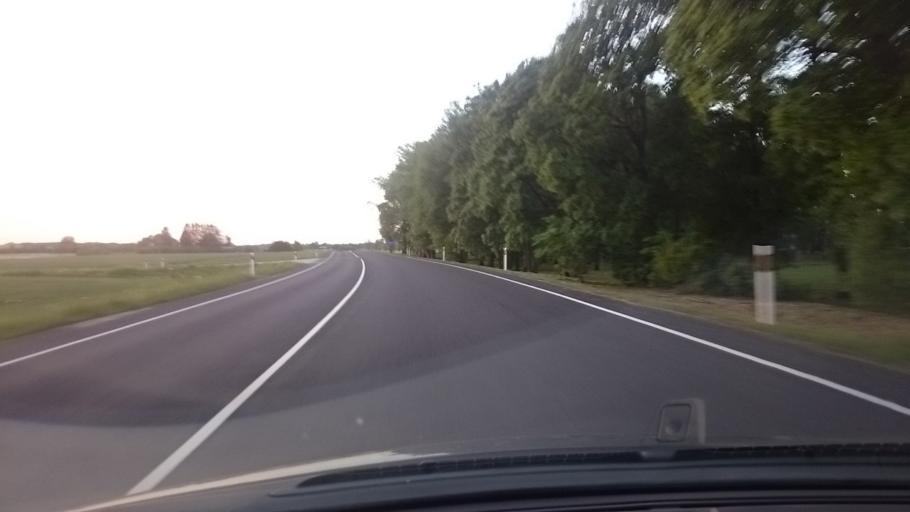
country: EE
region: Viljandimaa
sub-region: Vohma linn
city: Vohma
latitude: 58.6915
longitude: 25.6266
